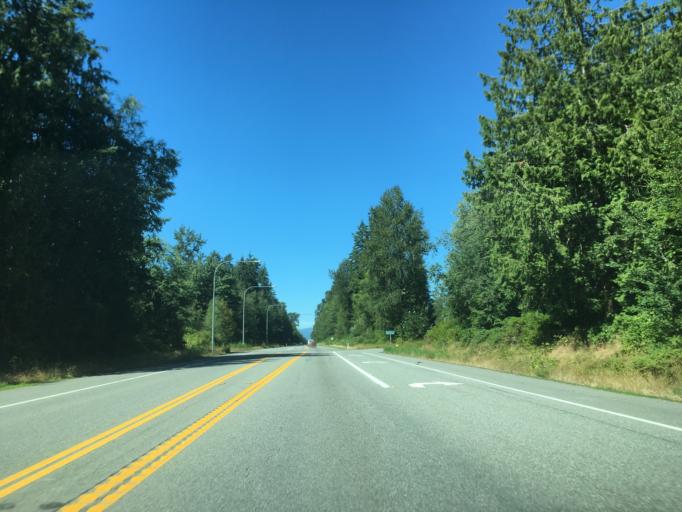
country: US
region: Washington
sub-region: Snohomish County
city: Sisco Heights
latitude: 48.1139
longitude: -122.1124
